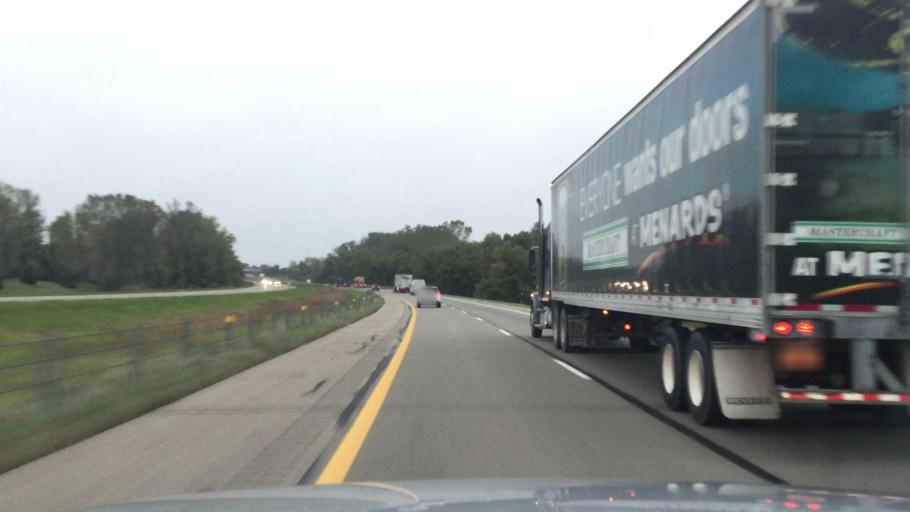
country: US
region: Michigan
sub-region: Shiawassee County
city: Durand
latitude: 42.9585
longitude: -83.9665
